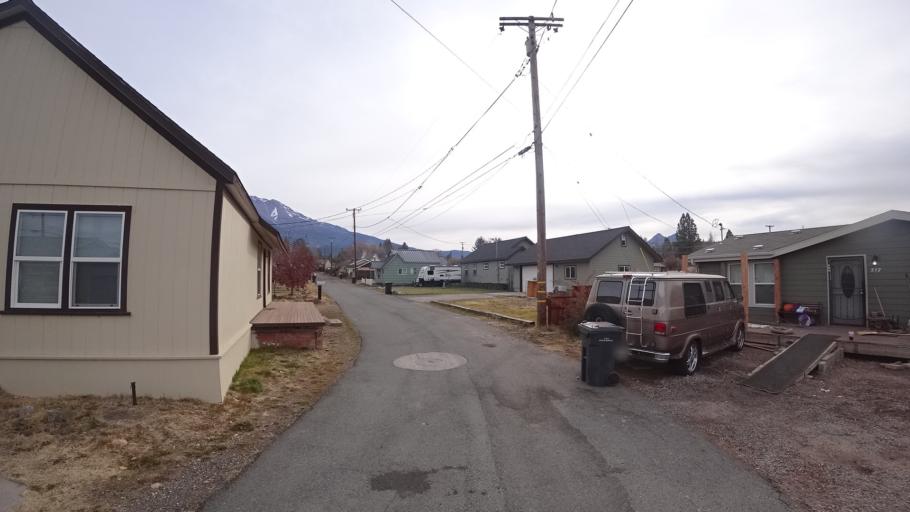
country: US
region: California
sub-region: Siskiyou County
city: Weed
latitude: 41.4308
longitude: -122.3778
